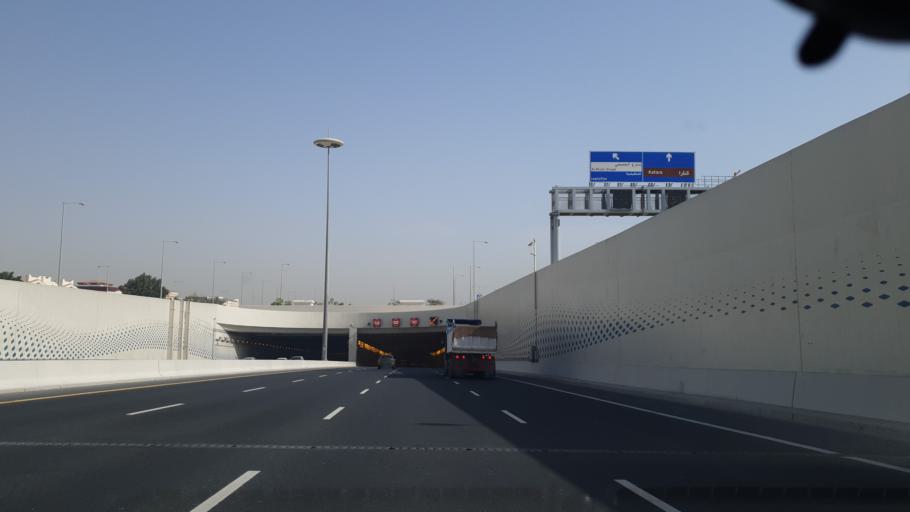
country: QA
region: Baladiyat ad Dawhah
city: Doha
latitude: 25.3483
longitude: 51.5204
